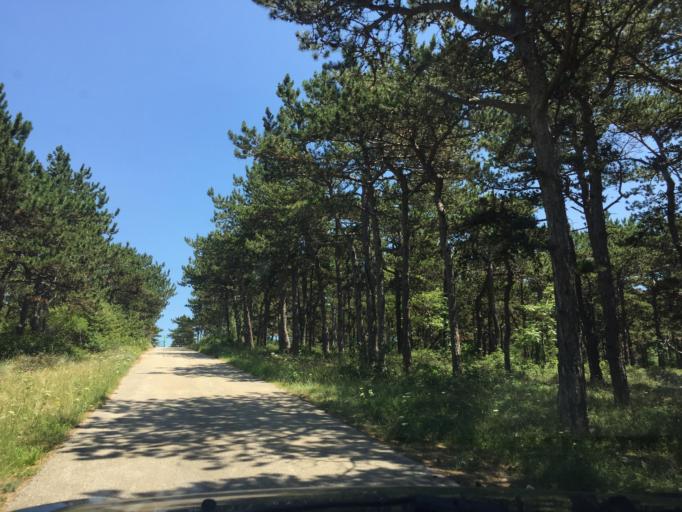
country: HR
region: Primorsko-Goranska
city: Punat
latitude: 45.0149
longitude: 14.6773
